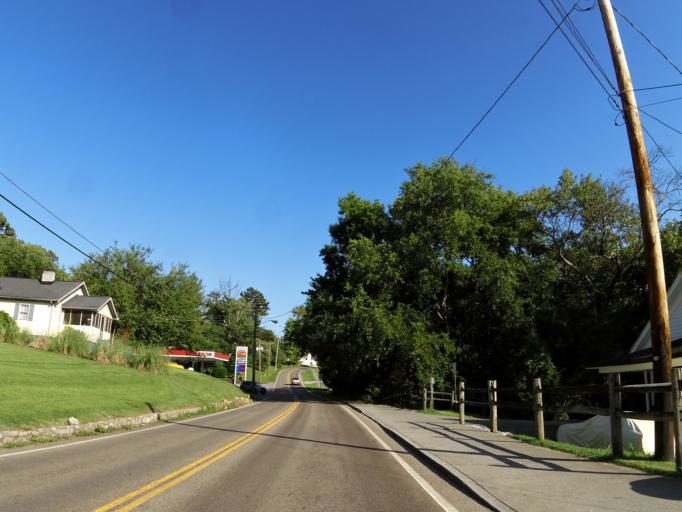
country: US
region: Tennessee
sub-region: Blount County
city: Maryville
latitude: 35.7490
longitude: -83.9718
